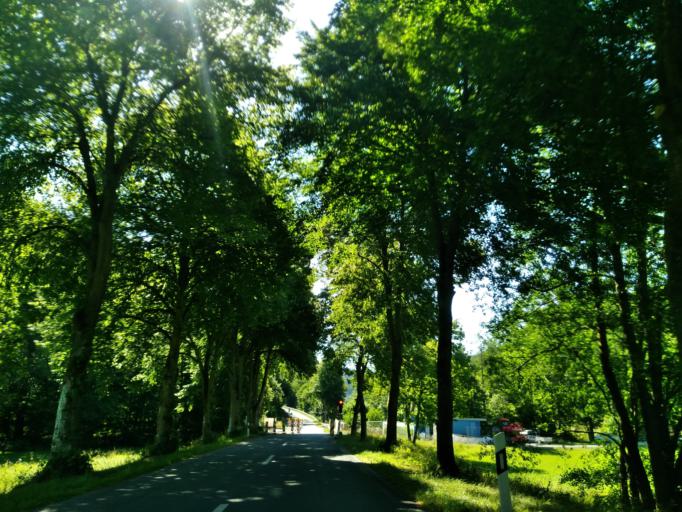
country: DE
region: Baden-Wuerttemberg
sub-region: Karlsruhe Region
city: Buchen
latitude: 49.5493
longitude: 9.2886
